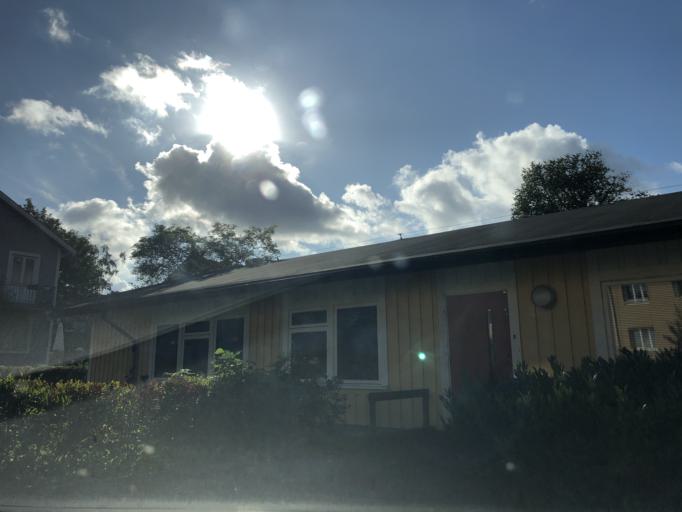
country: SE
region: Vaestra Goetaland
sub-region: Goteborg
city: Goeteborg
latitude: 57.7063
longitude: 11.9992
